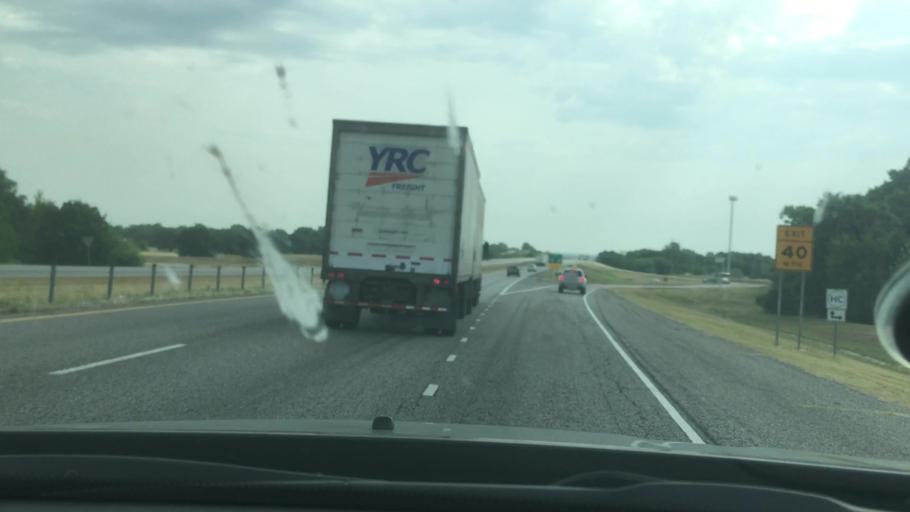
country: US
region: Oklahoma
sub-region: Bryan County
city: Durant
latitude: 34.0350
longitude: -96.3785
